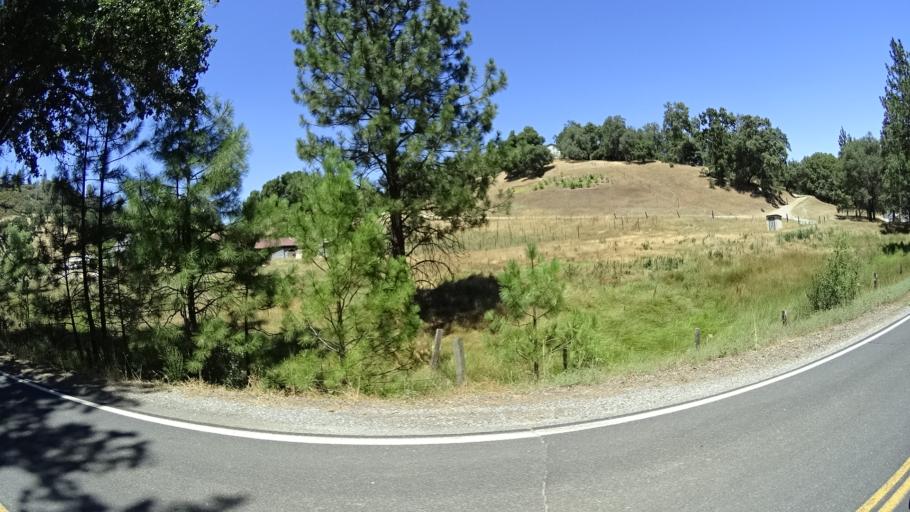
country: US
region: California
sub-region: Calaveras County
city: Mountain Ranch
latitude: 38.2868
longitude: -120.4980
